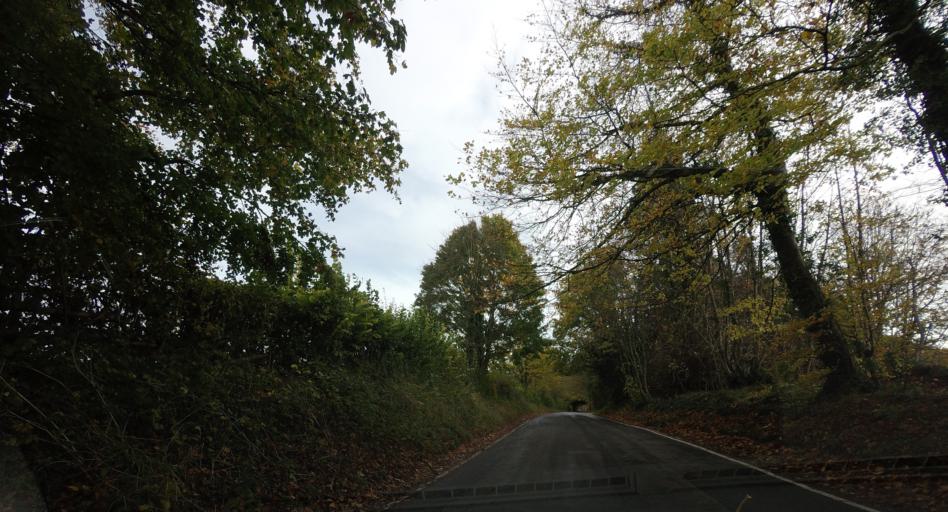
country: GB
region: England
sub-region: Kent
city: Shoreham
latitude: 51.3320
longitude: 0.1864
